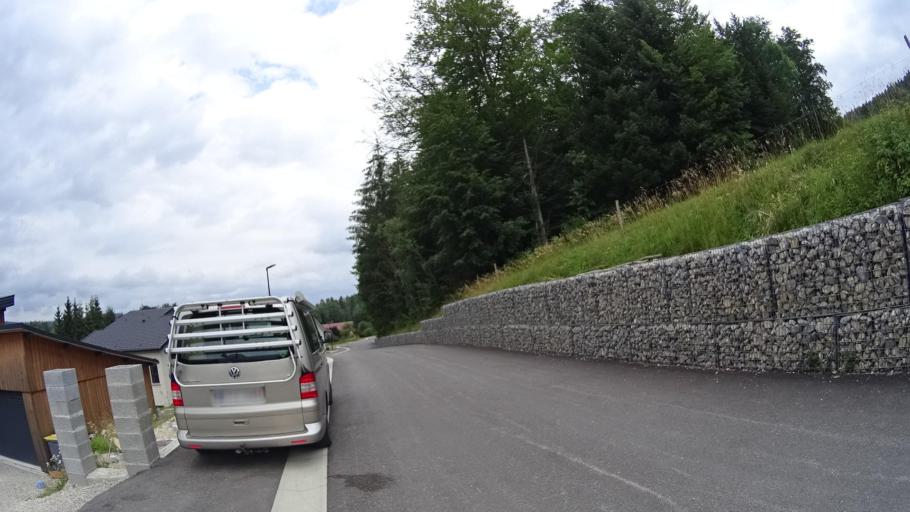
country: FR
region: Franche-Comte
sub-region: Departement du Doubs
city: Les Fourgs
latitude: 46.8179
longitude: 6.3298
